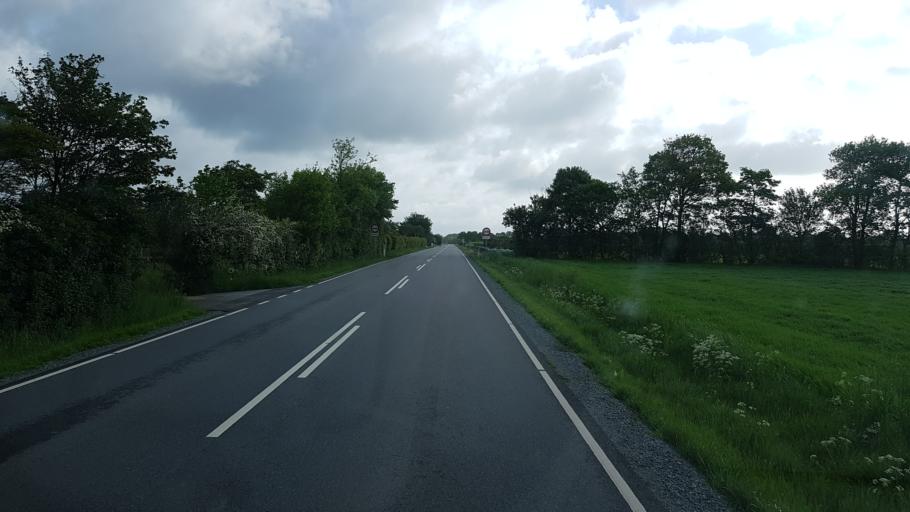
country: DK
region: South Denmark
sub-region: Vejen Kommune
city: Vejen
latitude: 55.4529
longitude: 9.1539
